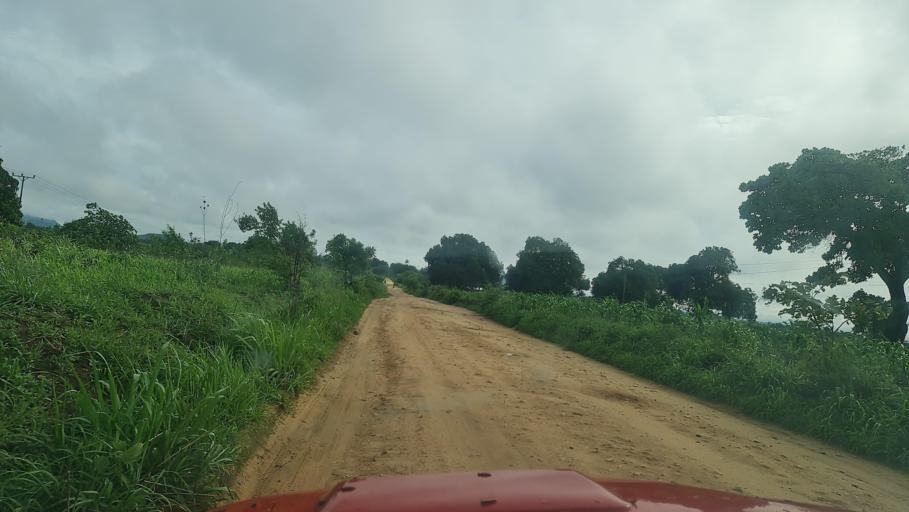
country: MW
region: Southern Region
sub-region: Nsanje District
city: Nsanje
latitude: -17.2930
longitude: 35.5978
